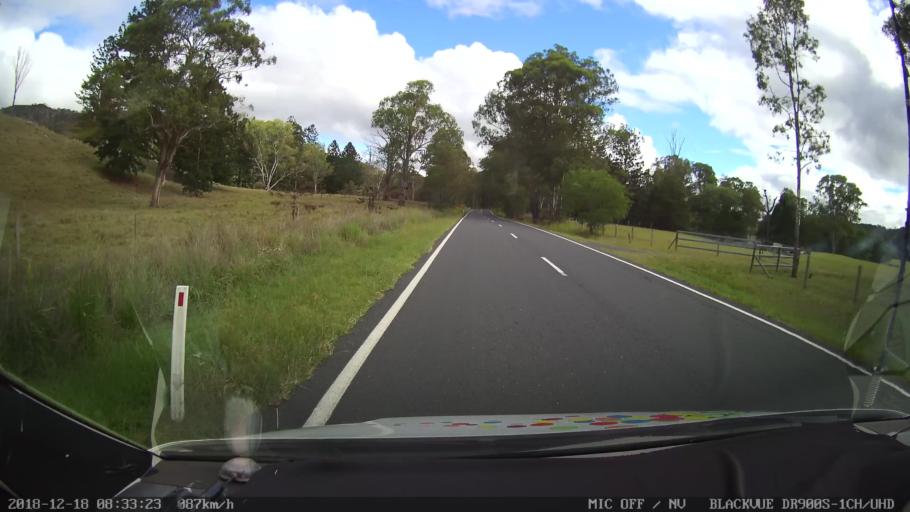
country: AU
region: New South Wales
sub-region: Kyogle
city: Kyogle
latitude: -28.2921
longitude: 152.7860
